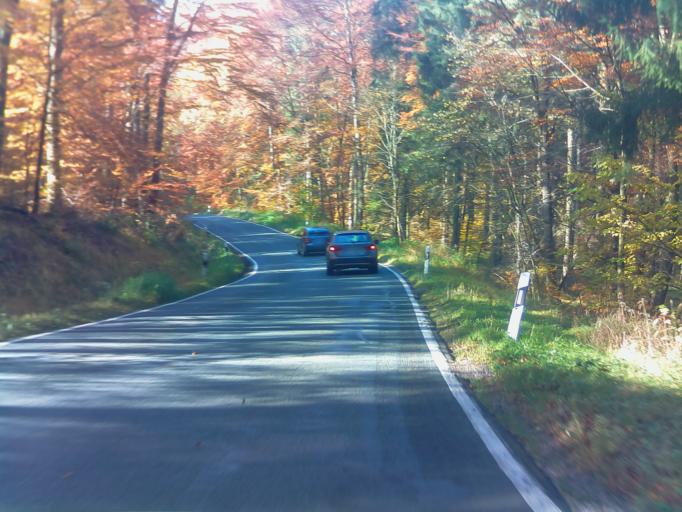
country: DE
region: Bavaria
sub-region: Regierungsbezirk Unterfranken
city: Michelau
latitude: 49.8593
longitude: 10.5029
